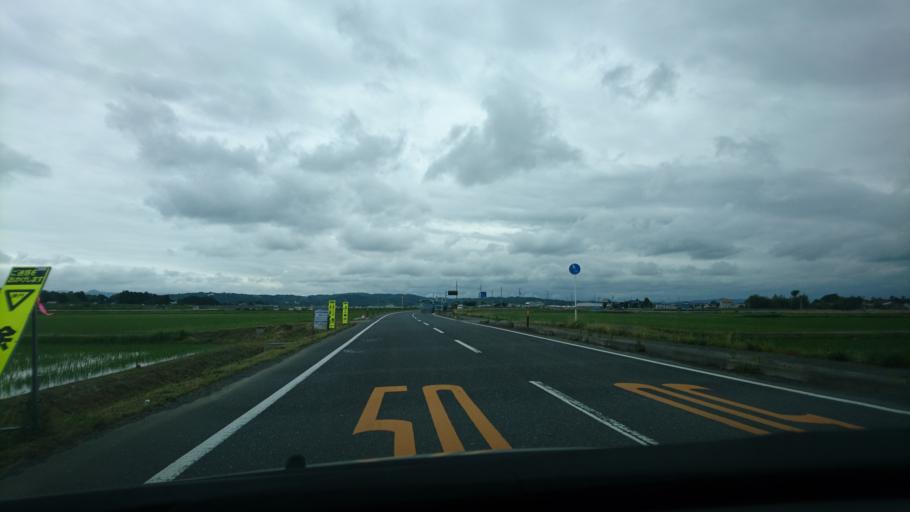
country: JP
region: Miyagi
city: Wakuya
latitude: 38.6809
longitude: 141.2611
